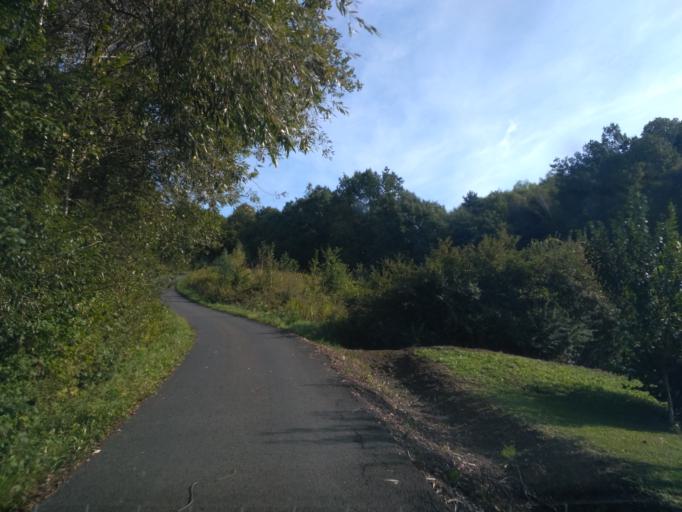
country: PL
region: Subcarpathian Voivodeship
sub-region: Powiat strzyzowski
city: Strzyzow
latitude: 49.8459
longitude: 21.8241
